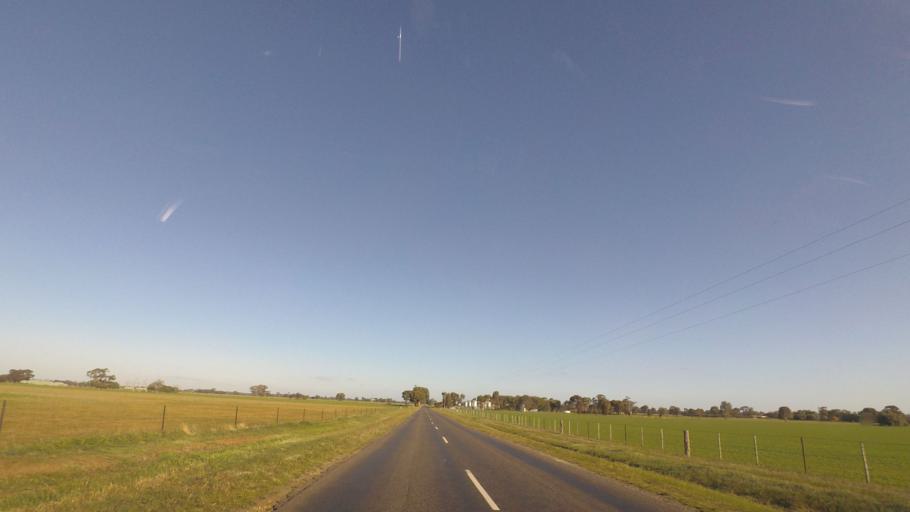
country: AU
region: Victoria
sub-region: Greater Bendigo
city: Epsom
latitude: -36.6133
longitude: 144.5346
